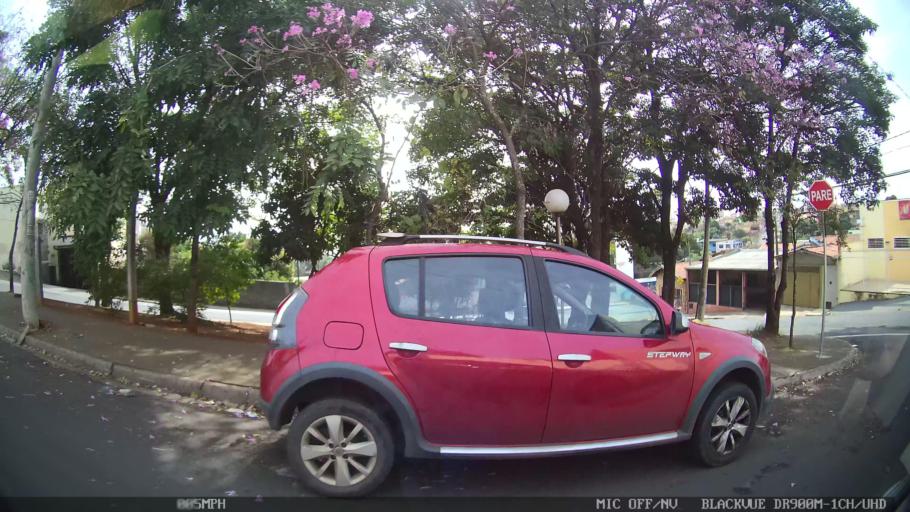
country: BR
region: Sao Paulo
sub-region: Piracicaba
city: Piracicaba
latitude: -22.7468
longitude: -47.6568
